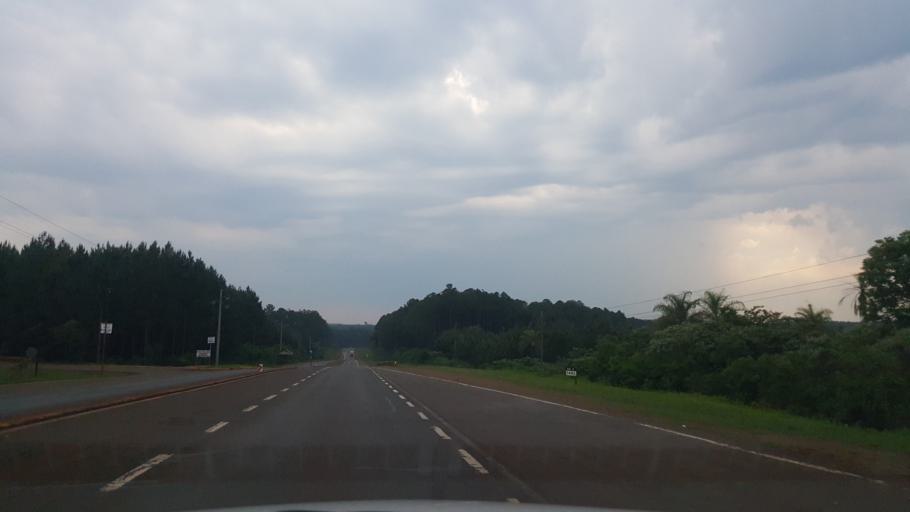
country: AR
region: Misiones
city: Jardin America
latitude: -27.0148
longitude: -55.1907
